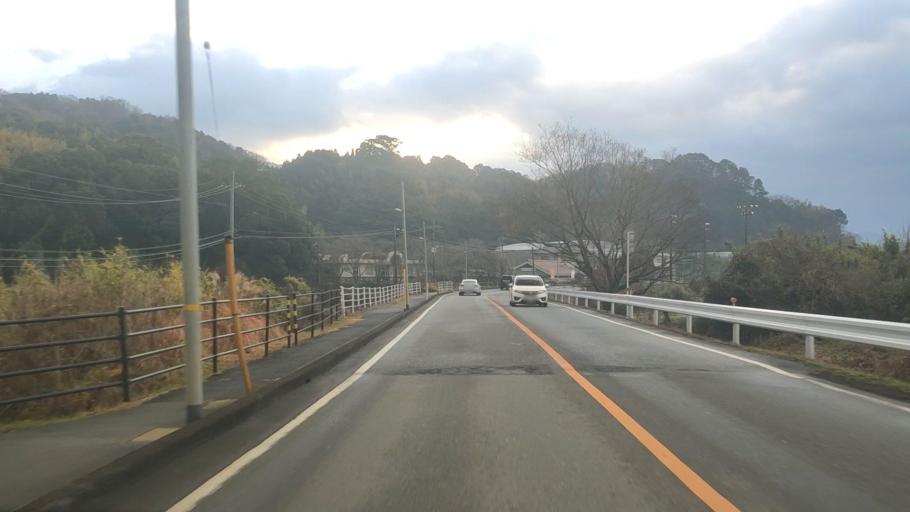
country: JP
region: Kumamoto
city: Uto
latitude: 32.6991
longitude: 130.7854
